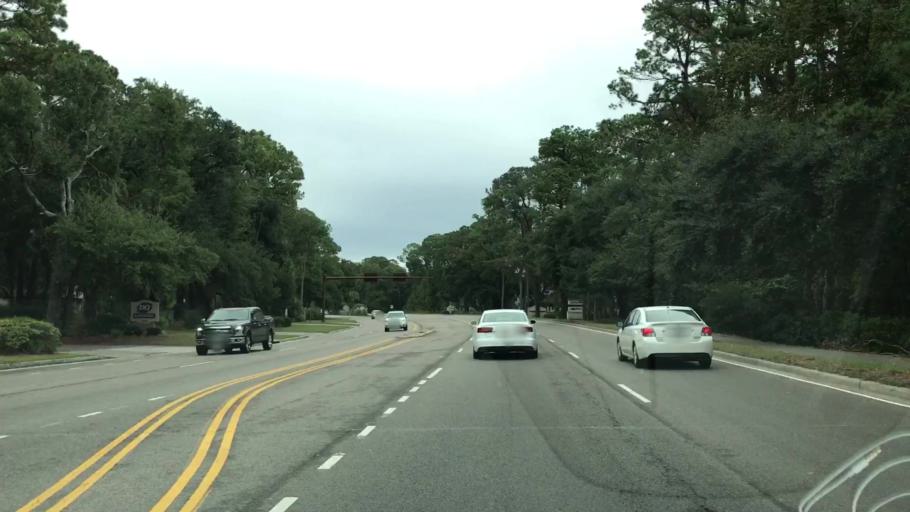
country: US
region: South Carolina
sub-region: Beaufort County
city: Hilton Head Island
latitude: 32.1567
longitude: -80.7585
